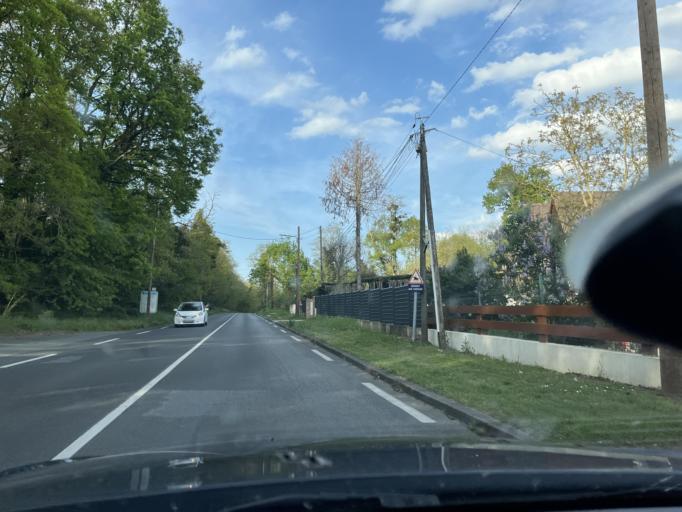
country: FR
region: Ile-de-France
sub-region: Departement de l'Essonne
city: Breuillet
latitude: 48.5622
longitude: 2.1549
